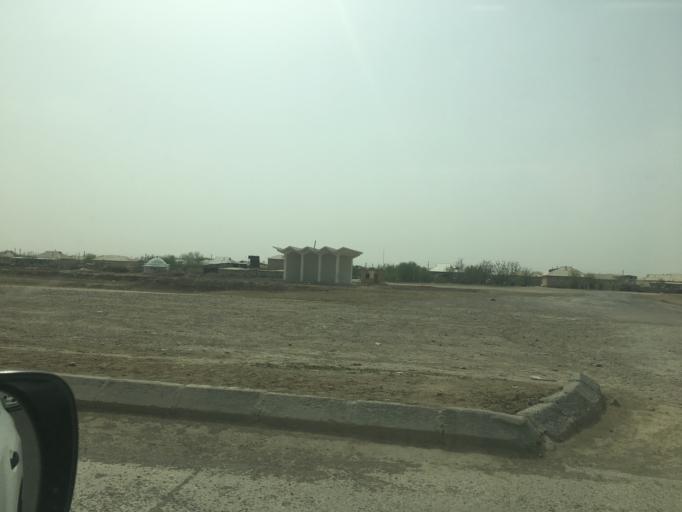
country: TM
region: Mary
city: Bayramaly
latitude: 37.5980
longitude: 62.1195
